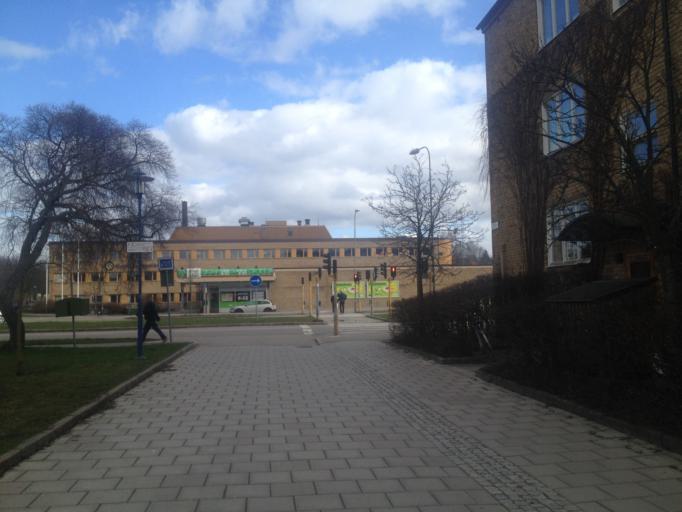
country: SE
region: Stockholm
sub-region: Stockholms Kommun
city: Arsta
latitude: 59.2831
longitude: 18.0712
